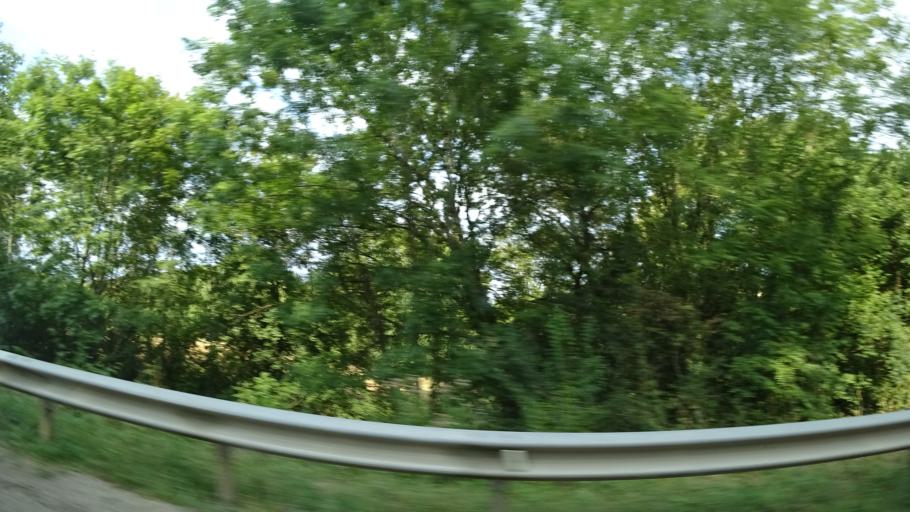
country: FR
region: Midi-Pyrenees
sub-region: Departement de l'Aveyron
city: Saint-Christophe-Vallon
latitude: 44.4931
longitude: 2.3878
